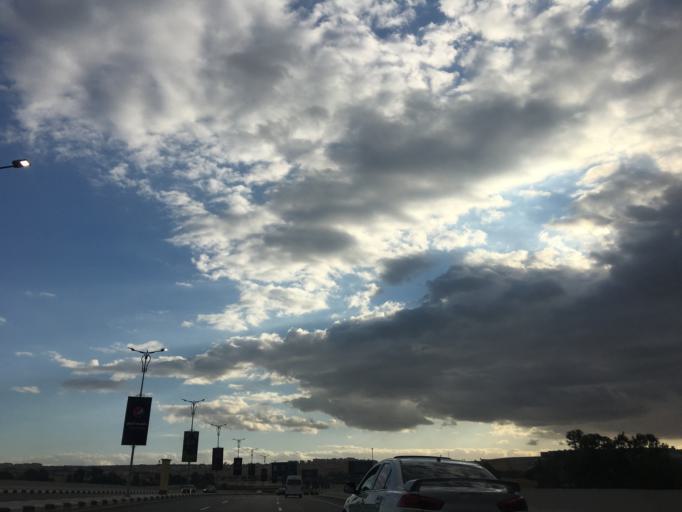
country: EG
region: Muhafazat al Qahirah
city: Cairo
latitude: 30.0430
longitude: 31.3079
